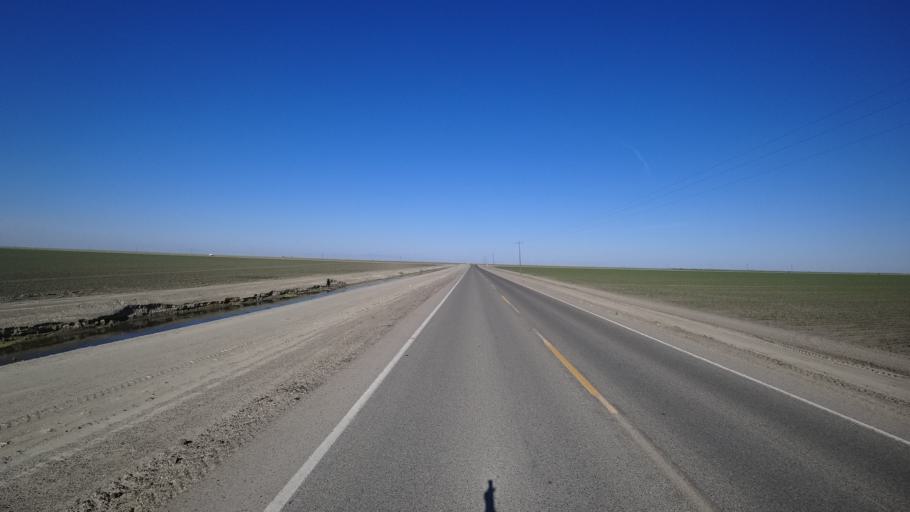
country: US
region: California
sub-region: Kings County
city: Corcoran
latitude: 36.0979
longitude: -119.6387
